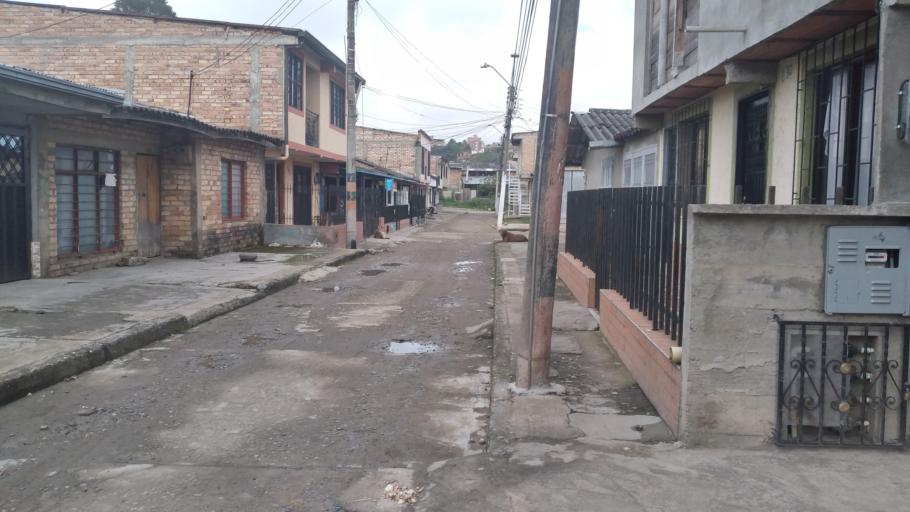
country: CO
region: Cauca
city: Popayan
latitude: 2.4293
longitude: -76.6105
